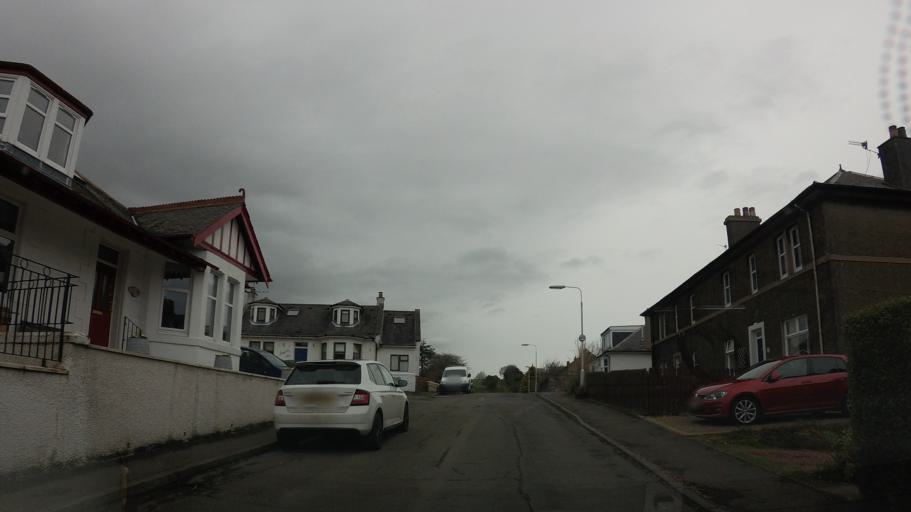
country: GB
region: Scotland
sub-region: Fife
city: Aberdour
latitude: 56.0581
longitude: -3.2967
